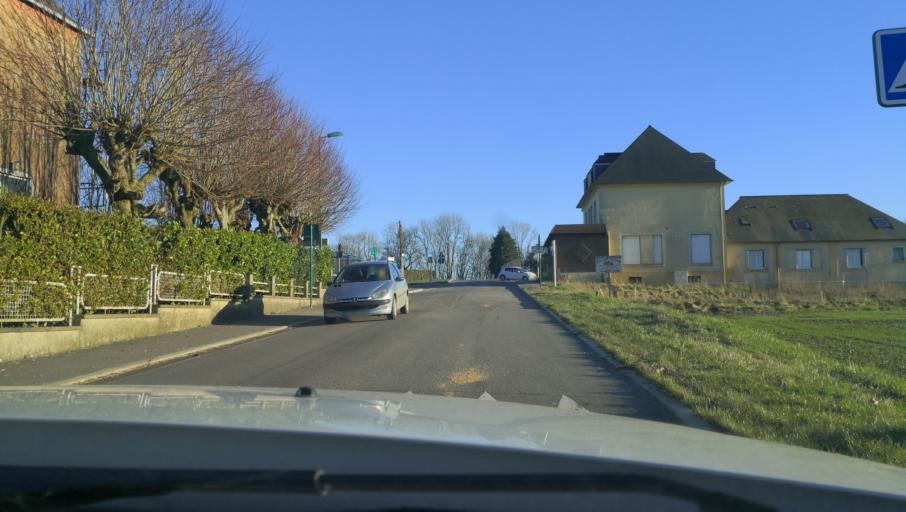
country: FR
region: Haute-Normandie
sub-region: Departement de la Seine-Maritime
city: Buchy
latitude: 49.6034
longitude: 1.3324
